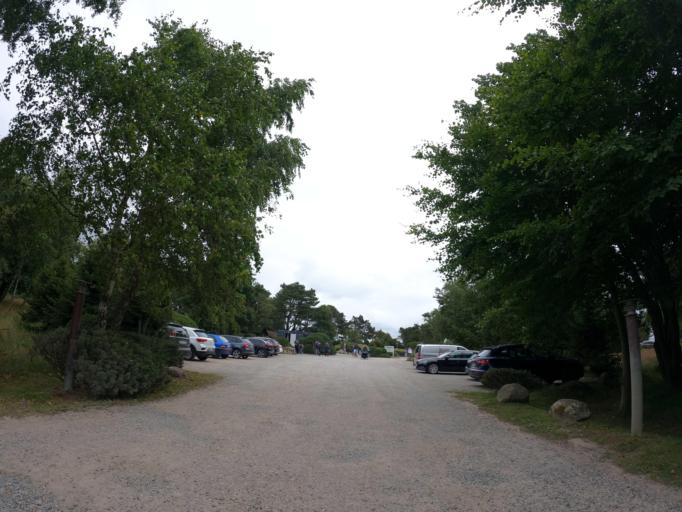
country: DE
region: Schleswig-Holstein
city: Tinnum
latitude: 54.9534
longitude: 8.3520
